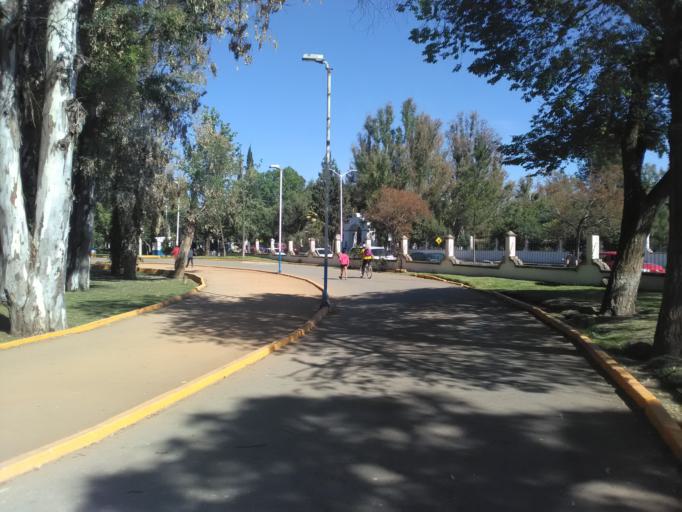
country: MX
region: Durango
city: Victoria de Durango
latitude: 24.0278
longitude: -104.6845
